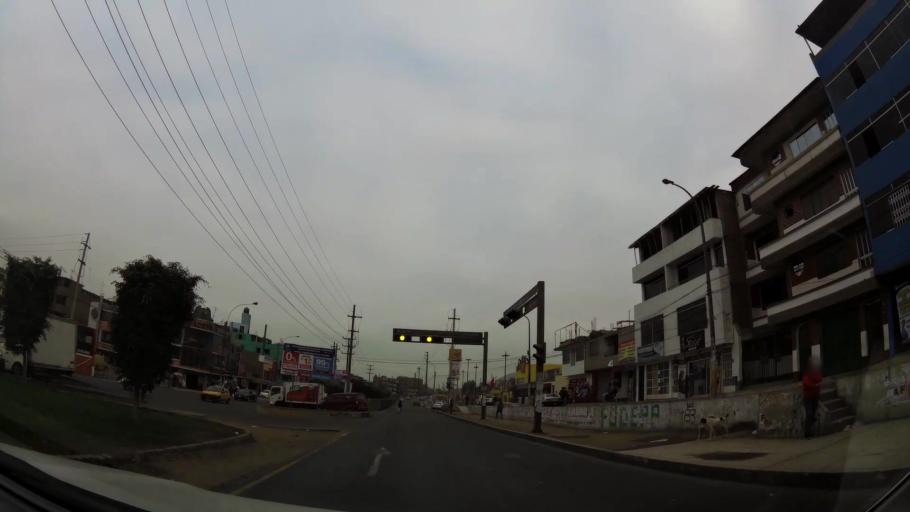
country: PE
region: Lima
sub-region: Lima
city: Independencia
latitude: -11.9899
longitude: -77.0154
